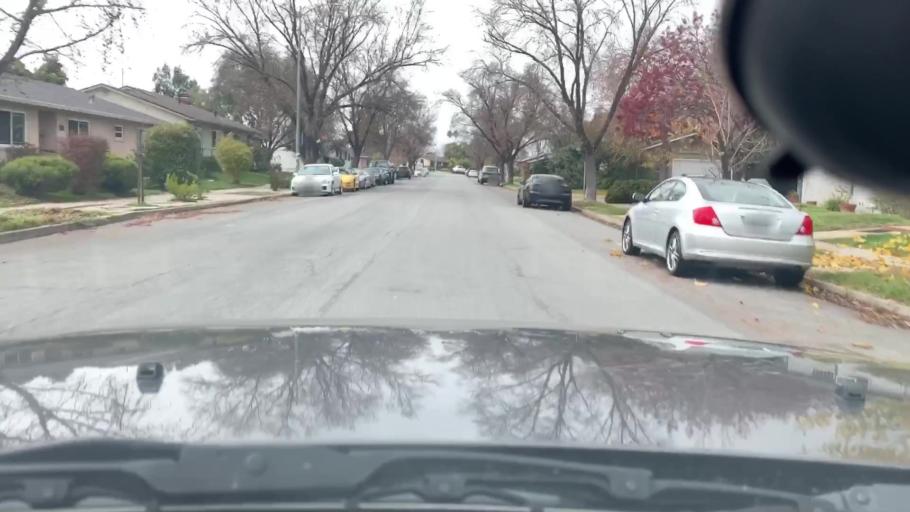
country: US
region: California
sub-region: Alameda County
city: Fremont
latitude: 37.5153
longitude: -121.9647
